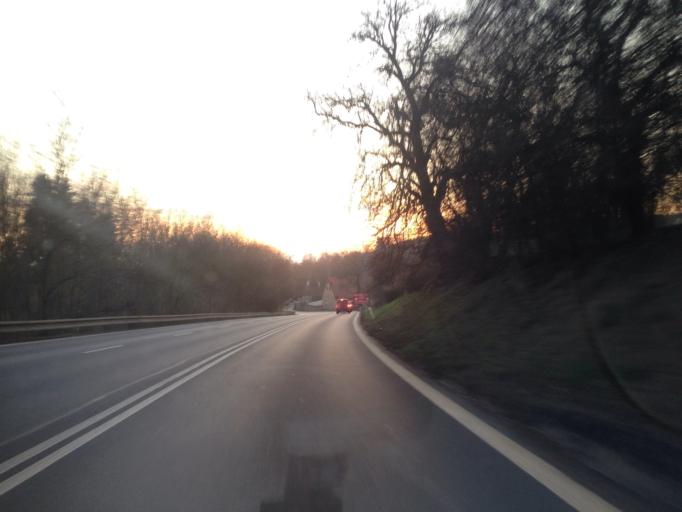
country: CZ
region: Central Bohemia
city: Revnicov
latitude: 50.1759
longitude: 13.7804
